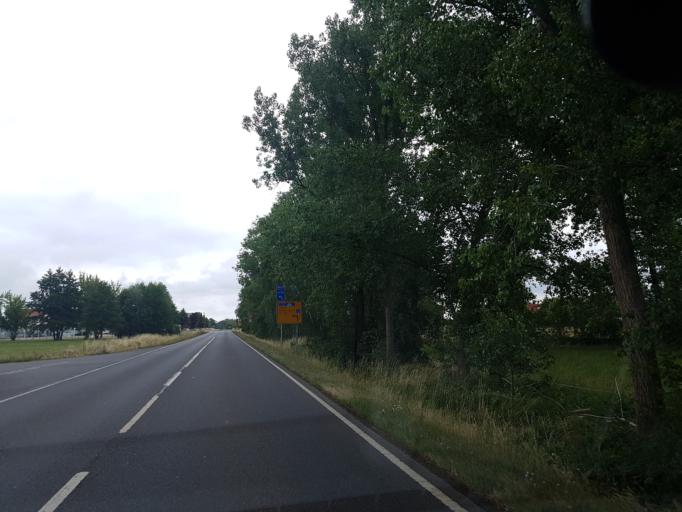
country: DE
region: Brandenburg
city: Luckau
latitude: 51.8577
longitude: 13.7348
